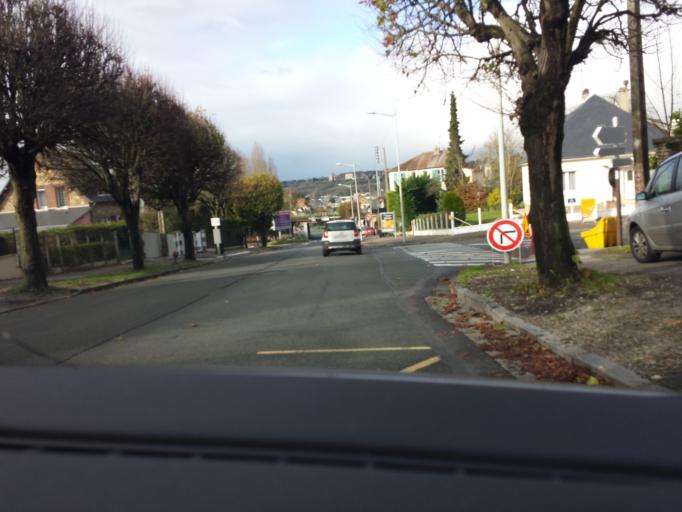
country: FR
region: Haute-Normandie
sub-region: Departement de l'Eure
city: Evreux
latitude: 49.0200
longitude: 1.1601
